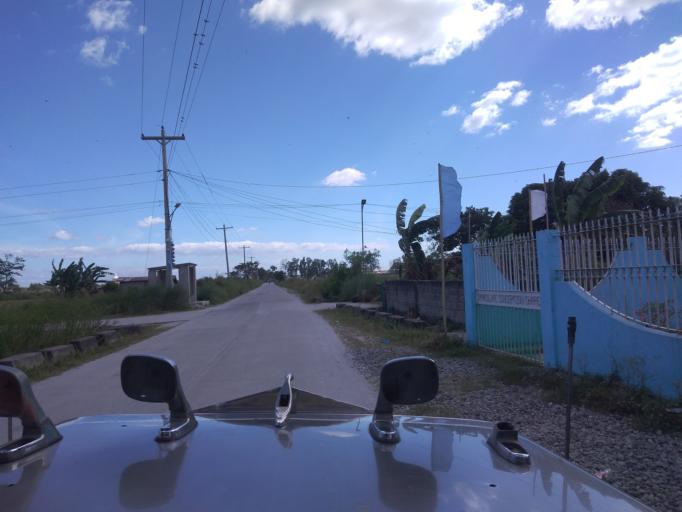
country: PH
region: Central Luzon
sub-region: Province of Pampanga
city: Magliman
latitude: 15.0435
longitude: 120.6292
